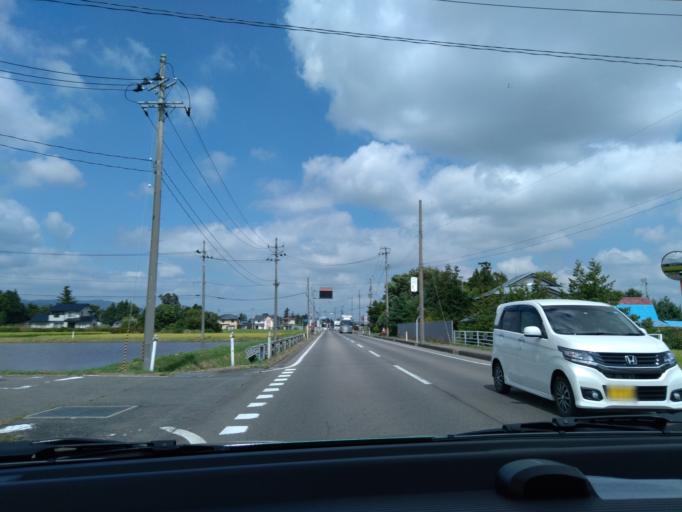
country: JP
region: Iwate
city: Hanamaki
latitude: 39.4410
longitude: 141.0980
